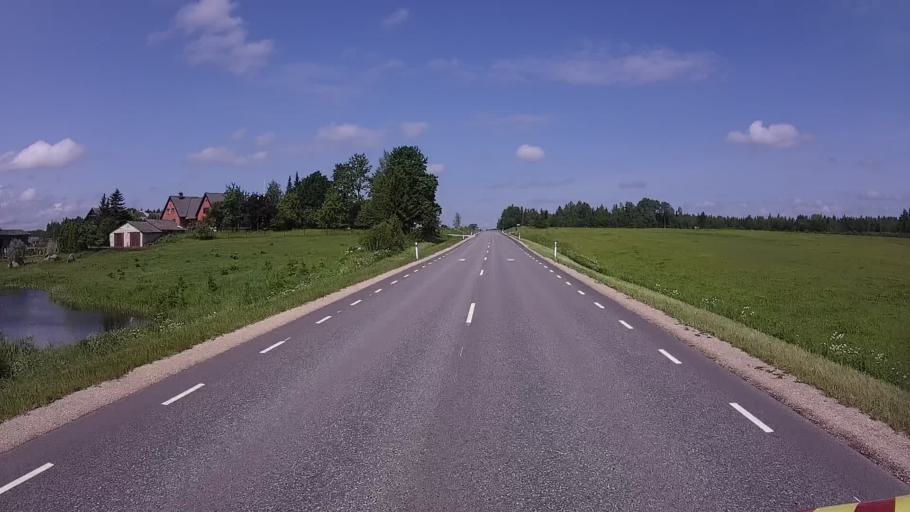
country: EE
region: Polvamaa
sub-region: Polva linn
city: Polva
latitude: 58.1716
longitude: 26.9086
